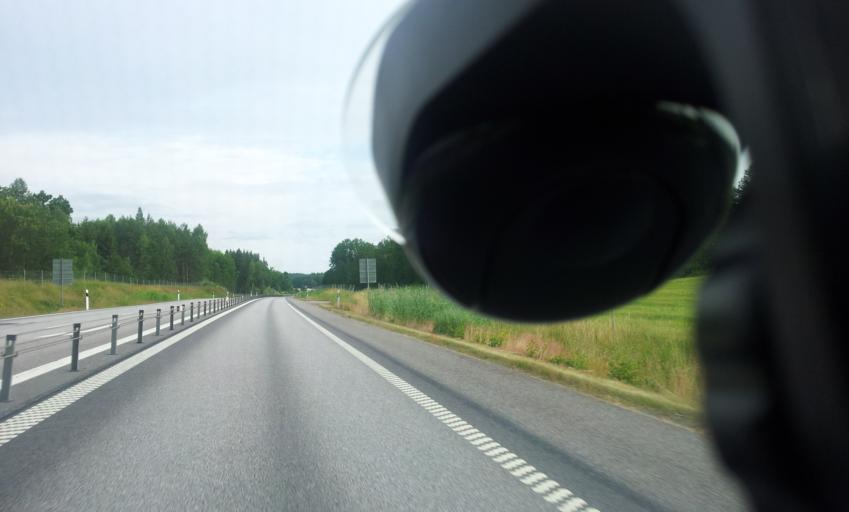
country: SE
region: OEstergoetland
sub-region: Valdemarsviks Kommun
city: Gusum
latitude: 58.3685
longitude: 16.4294
